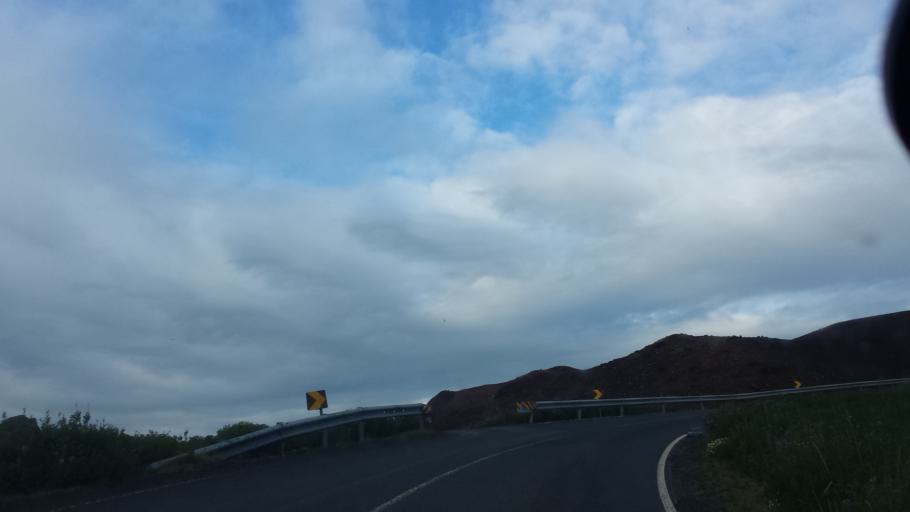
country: IS
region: South
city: Vestmannaeyjar
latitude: 63.4438
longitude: -20.2589
